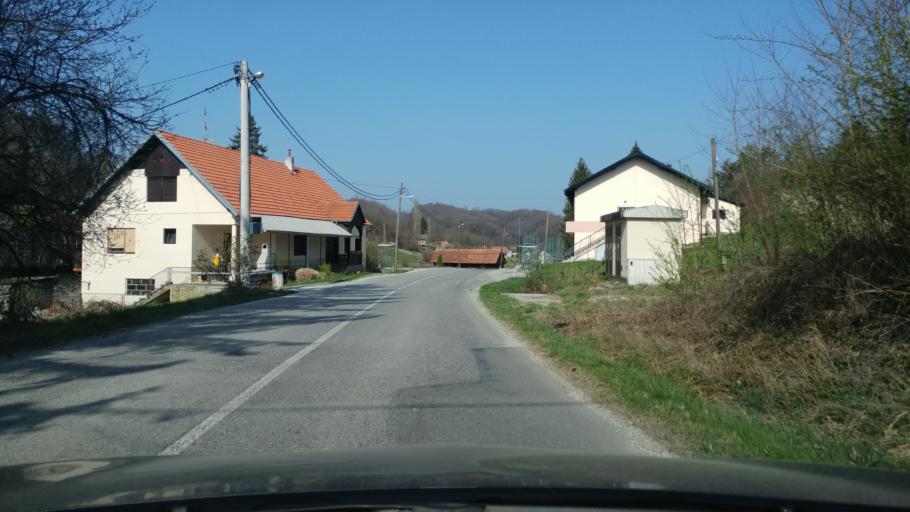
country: HR
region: Zagrebacka
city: Pojatno
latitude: 45.9427
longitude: 15.7533
